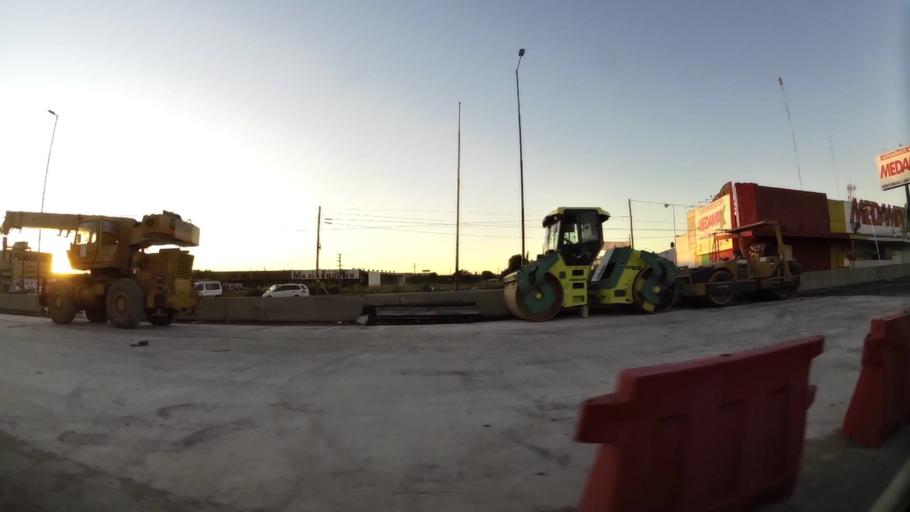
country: AR
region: Buenos Aires
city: Pontevedra
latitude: -34.7436
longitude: -58.6083
